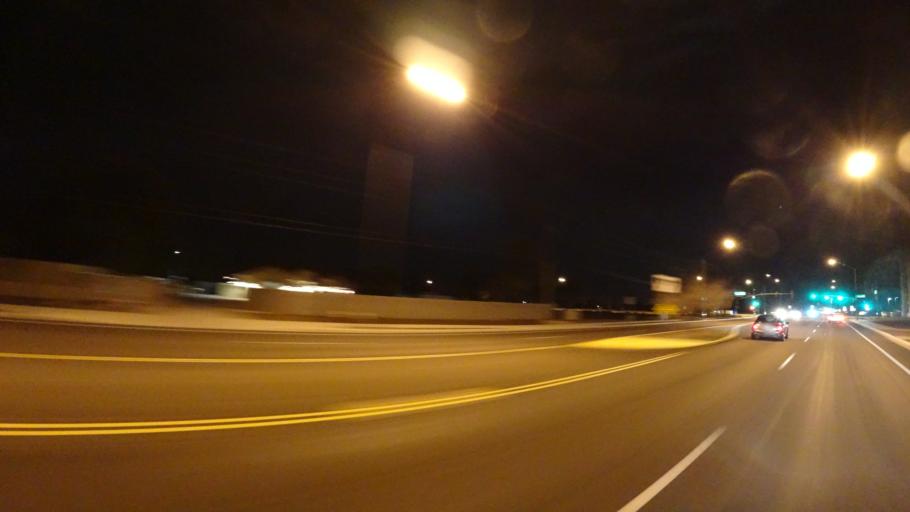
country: US
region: Arizona
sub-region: Maricopa County
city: Queen Creek
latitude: 33.2632
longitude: -111.7365
